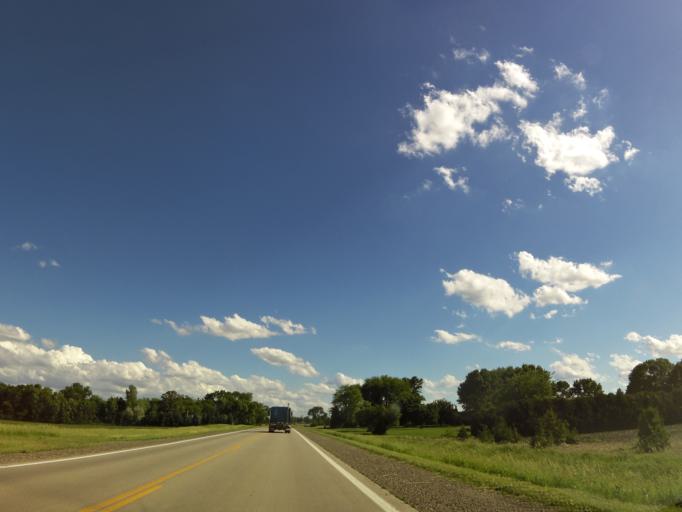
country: US
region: Minnesota
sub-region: McLeod County
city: Winsted
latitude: 44.9150
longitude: -94.1855
